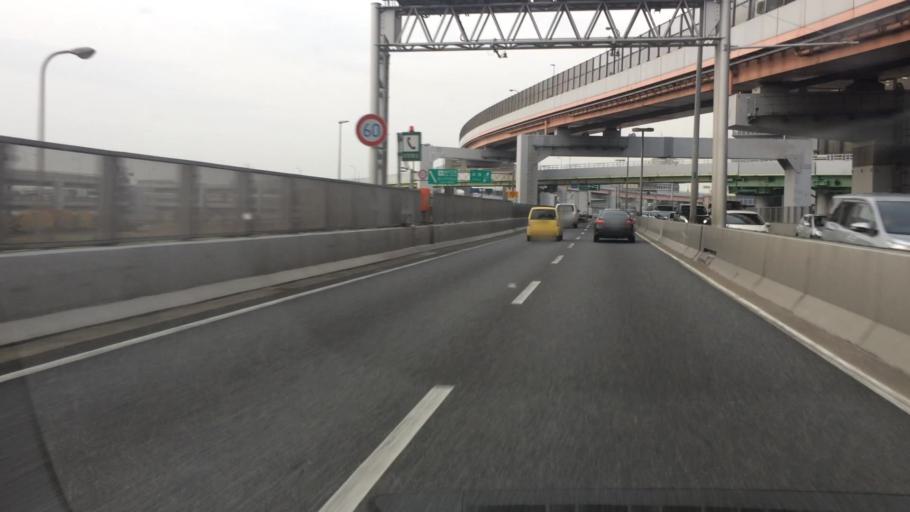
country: JP
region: Hyogo
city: Kobe
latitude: 34.6889
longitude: 135.2010
